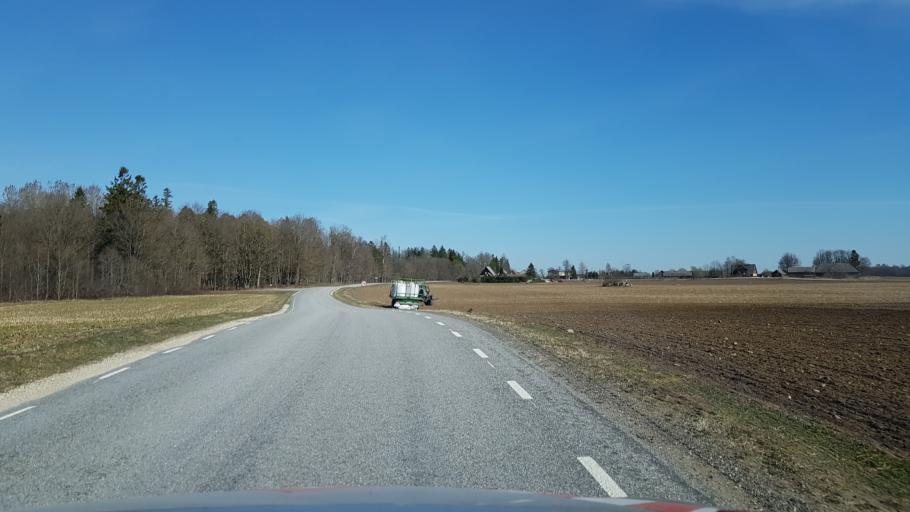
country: EE
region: Laeaene-Virumaa
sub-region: Vinni vald
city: Vinni
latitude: 59.2616
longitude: 26.3625
